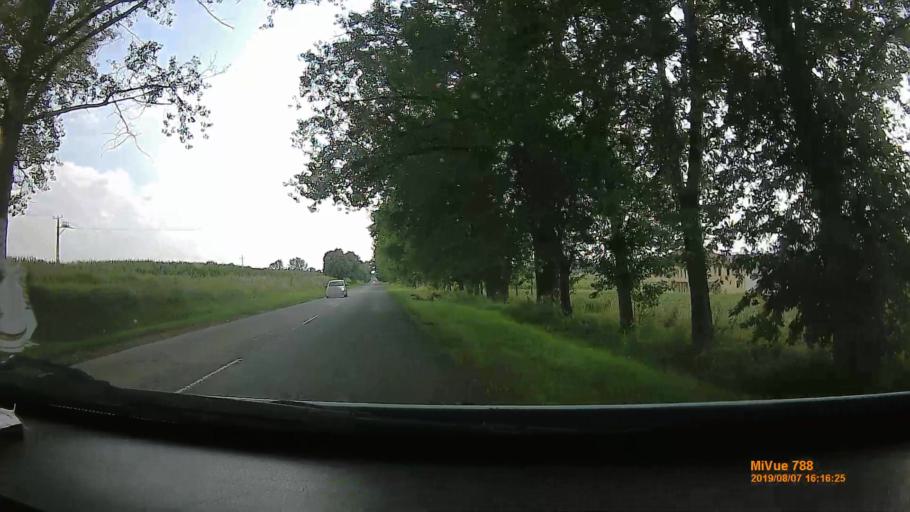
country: HU
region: Borsod-Abauj-Zemplen
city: Gonc
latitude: 48.4619
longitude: 21.2487
